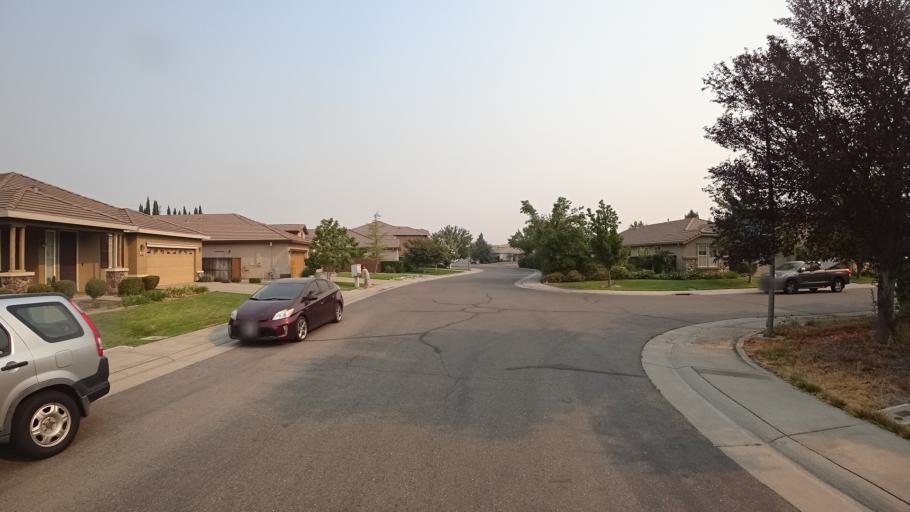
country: US
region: California
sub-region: Sacramento County
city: Laguna
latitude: 38.4001
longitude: -121.4502
